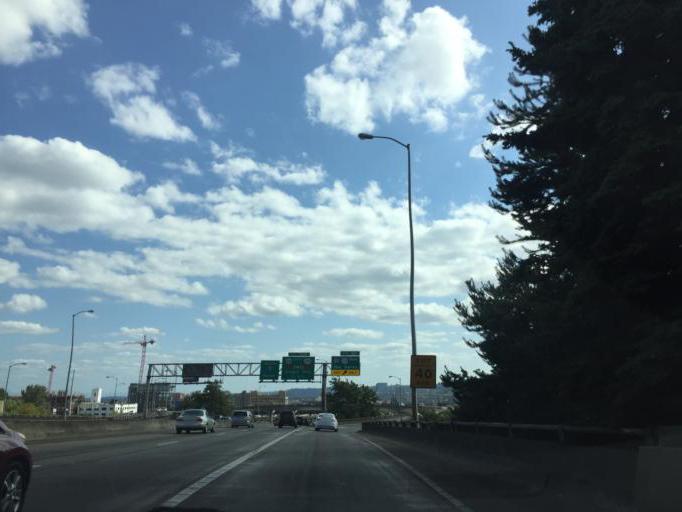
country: US
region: Oregon
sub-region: Multnomah County
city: Portland
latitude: 45.5291
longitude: -122.6654
